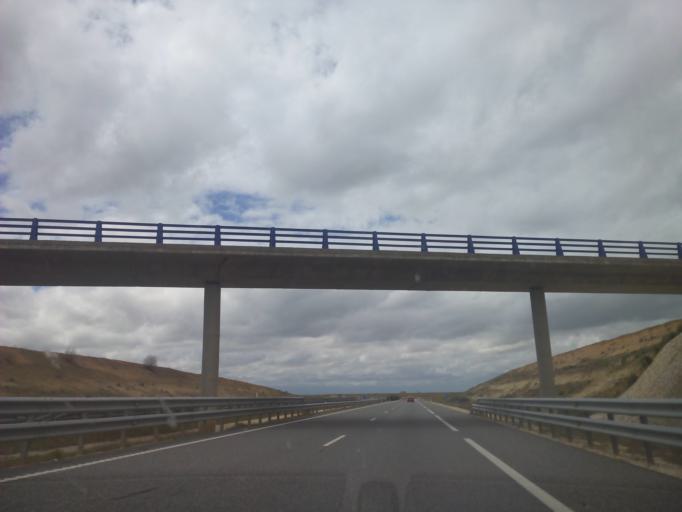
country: ES
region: Castille and Leon
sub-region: Provincia de Salamanca
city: Calvarrasa de Abajo
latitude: 40.9303
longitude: -5.5492
